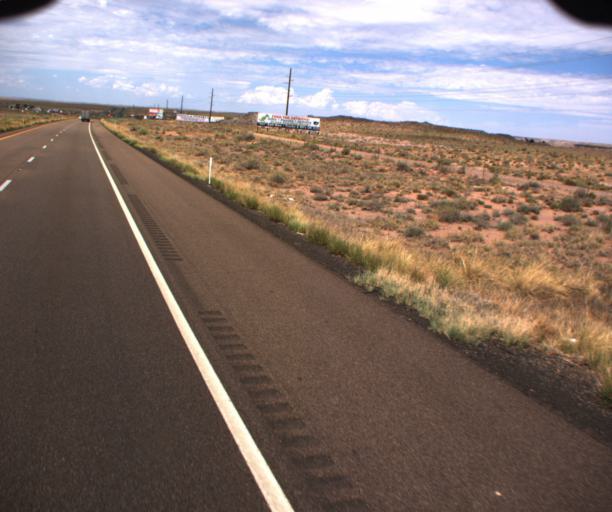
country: US
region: Arizona
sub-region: Navajo County
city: Holbrook
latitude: 35.0029
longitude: -109.8897
